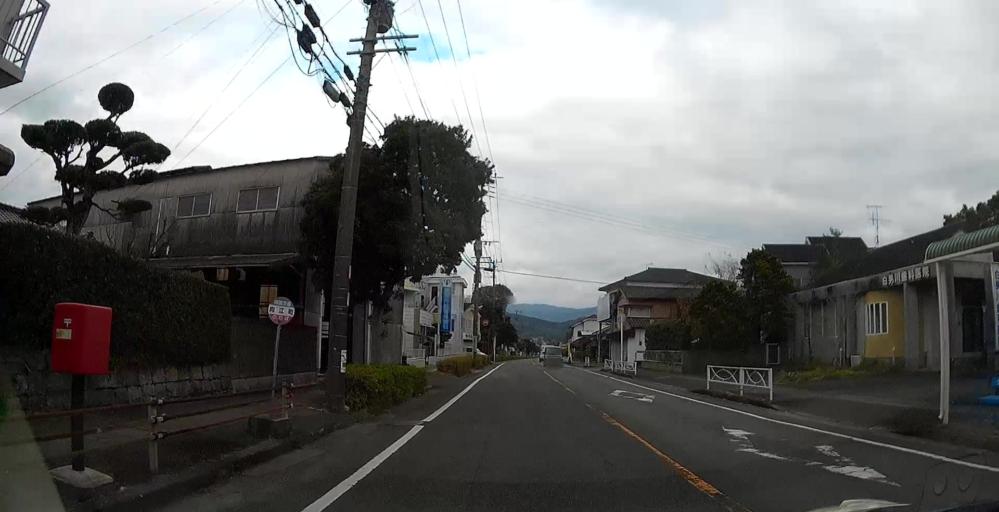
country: JP
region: Kagoshima
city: Izumi
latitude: 32.0762
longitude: 130.3513
